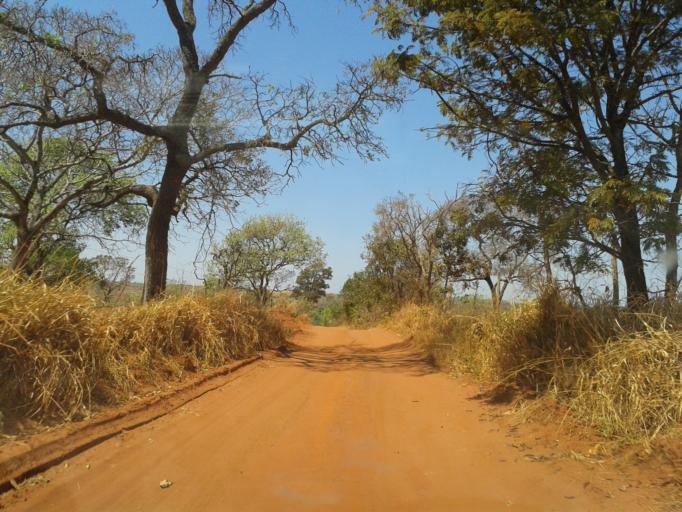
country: BR
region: Minas Gerais
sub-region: Ituiutaba
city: Ituiutaba
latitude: -19.0627
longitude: -49.3536
